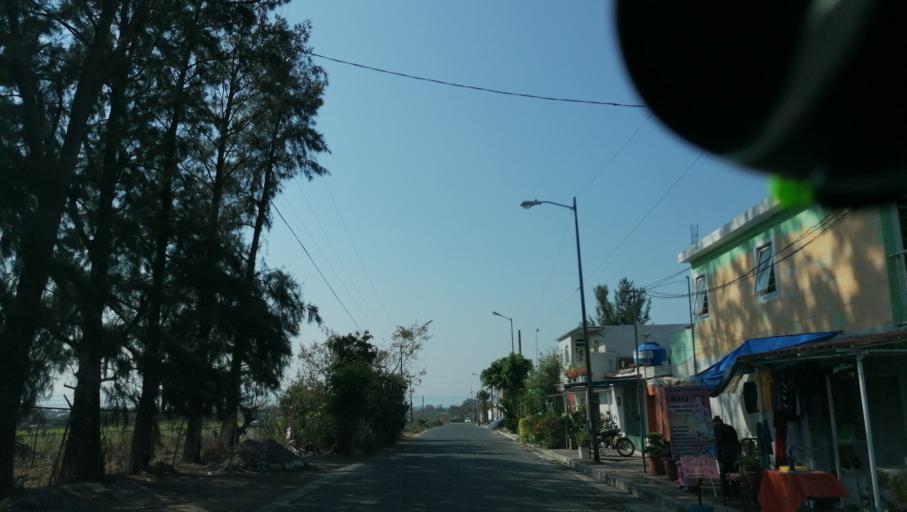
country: MX
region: Puebla
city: Atlixco
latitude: 18.9304
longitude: -98.4573
